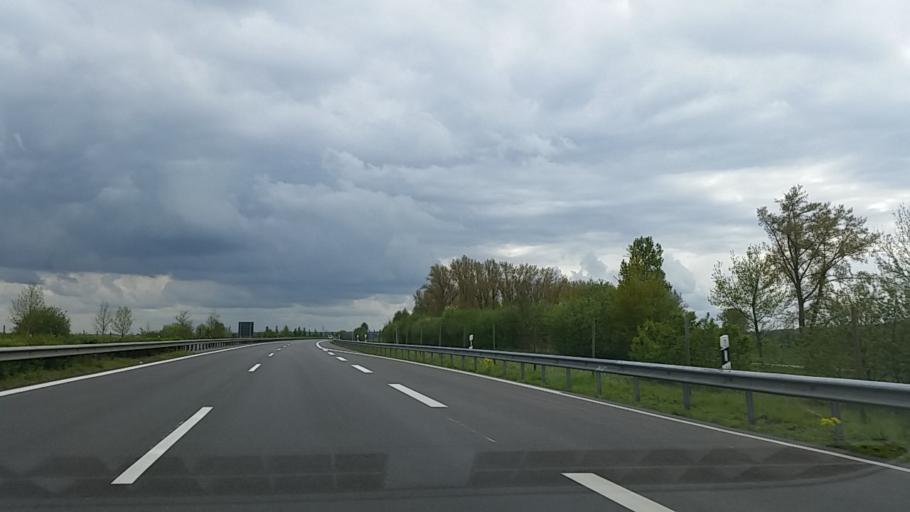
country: DE
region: Lower Saxony
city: Dollern
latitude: 53.5418
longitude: 9.5733
